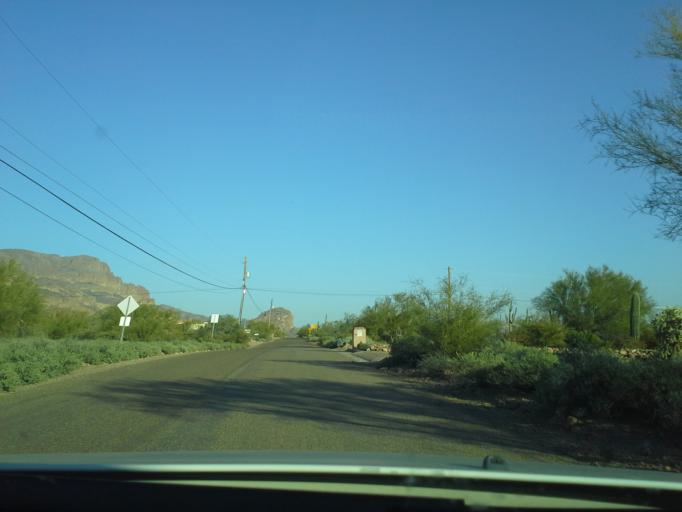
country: US
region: Arizona
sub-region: Pinal County
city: Apache Junction
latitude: 33.3898
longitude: -111.4347
